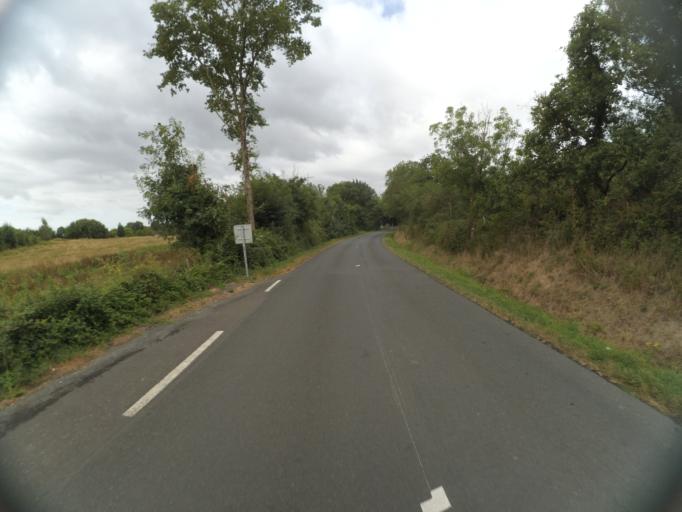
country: FR
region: Pays de la Loire
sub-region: Departement de la Vendee
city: La Bernardiere
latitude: 47.0562
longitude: -1.2618
